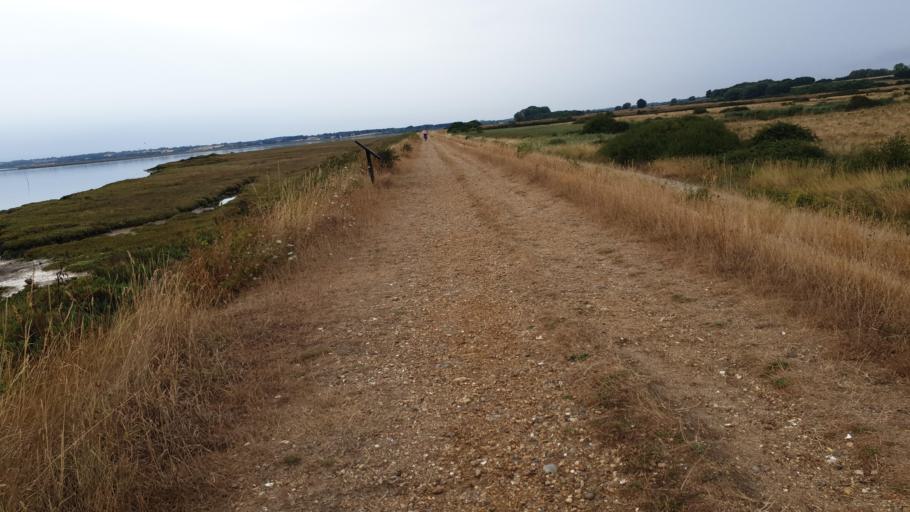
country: GB
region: England
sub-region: Essex
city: Brightlingsea
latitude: 51.8119
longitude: 1.0020
